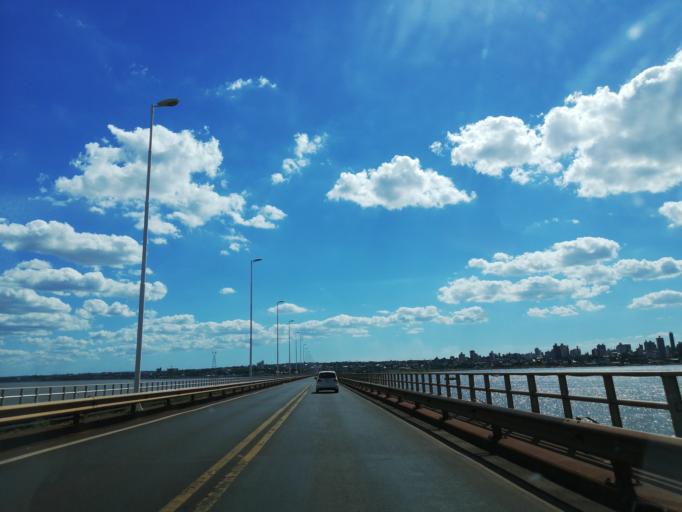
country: AR
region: Misiones
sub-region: Departamento de Capital
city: Posadas
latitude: -27.3720
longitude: -55.8687
